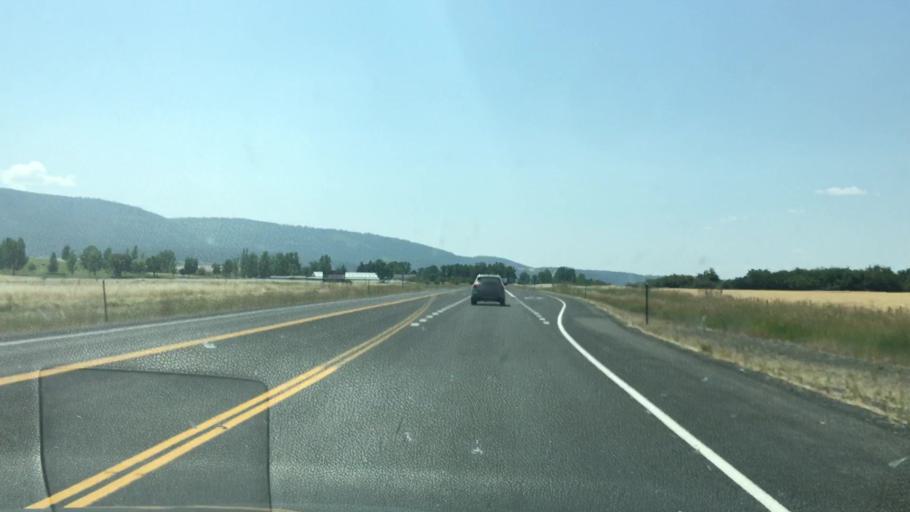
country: US
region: Idaho
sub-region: Idaho County
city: Grangeville
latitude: 45.9192
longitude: -116.1560
